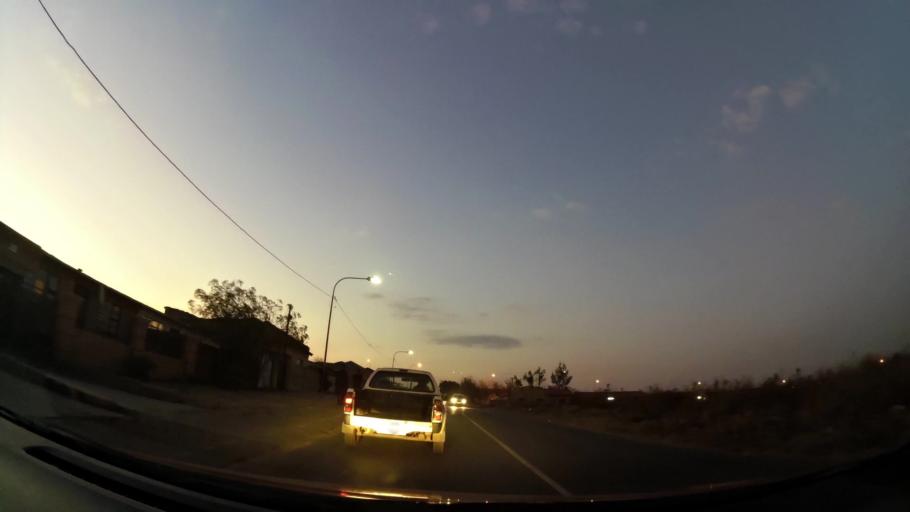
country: ZA
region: Gauteng
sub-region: City of Johannesburg Metropolitan Municipality
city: Soweto
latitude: -26.2221
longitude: 27.9089
